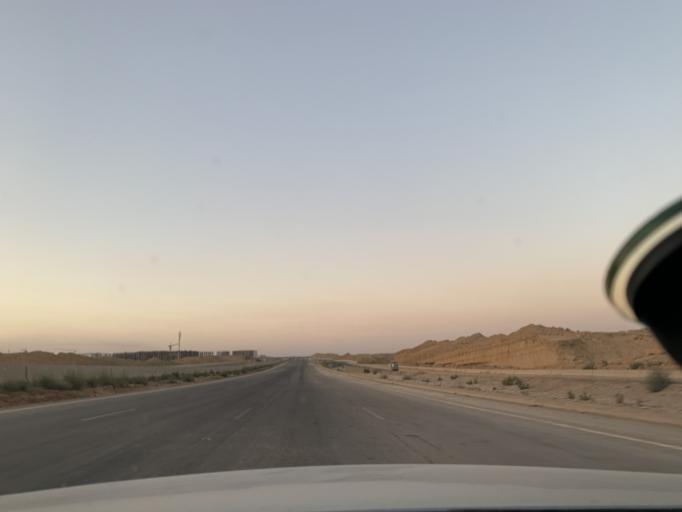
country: EG
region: Muhafazat al Qahirah
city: Halwan
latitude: 29.9582
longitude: 31.5439
